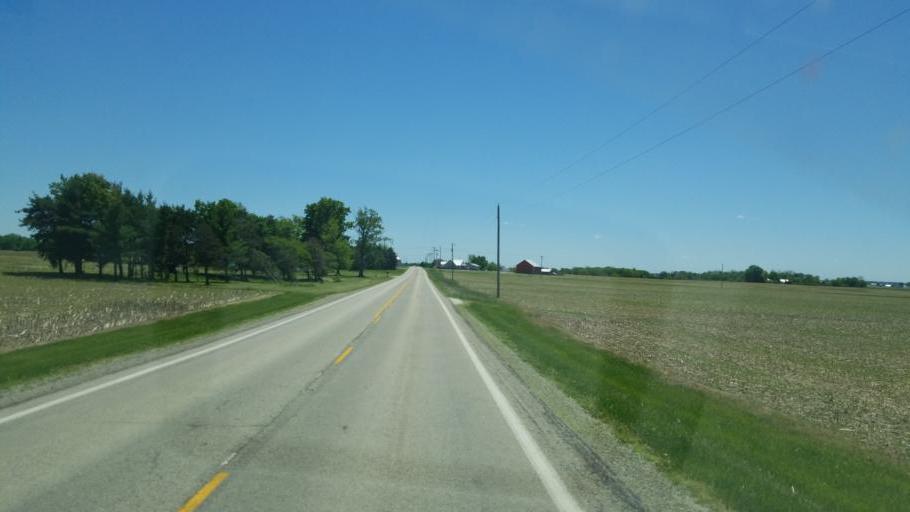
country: US
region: Ohio
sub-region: Darke County
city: Ansonia
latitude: 40.2678
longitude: -84.7021
